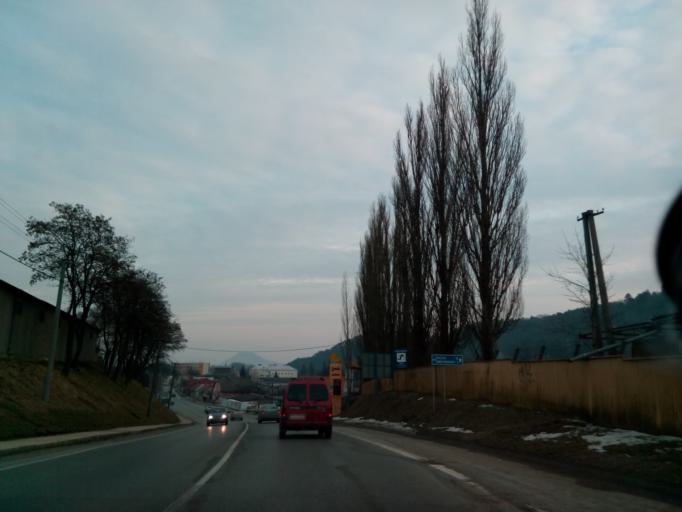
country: SK
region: Presovsky
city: Sabinov
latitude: 49.1075
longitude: 21.0849
